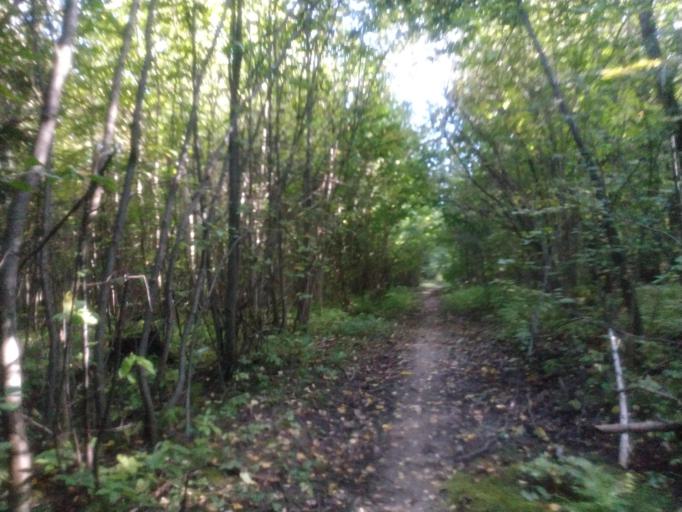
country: RU
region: Chuvashia
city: Novyye Lapsary
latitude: 56.1344
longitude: 47.1110
